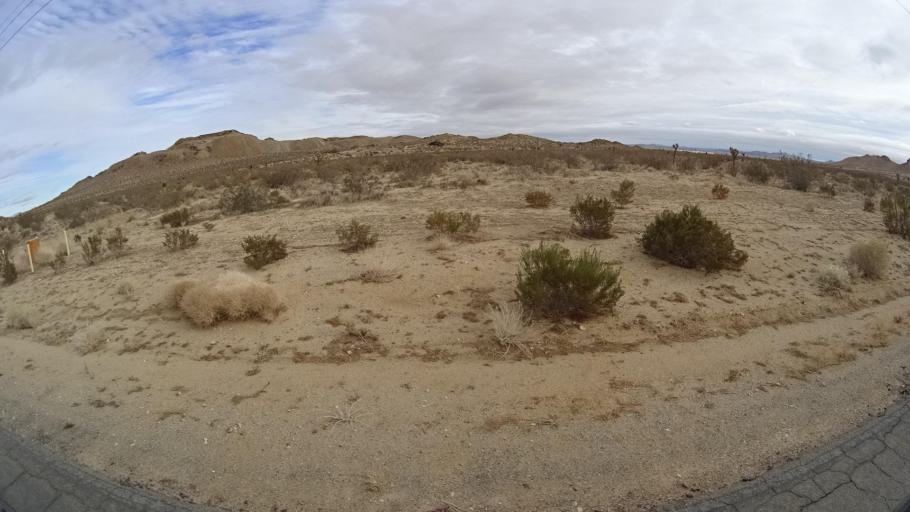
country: US
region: California
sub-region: Kern County
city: Mojave
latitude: 35.0009
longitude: -118.1863
